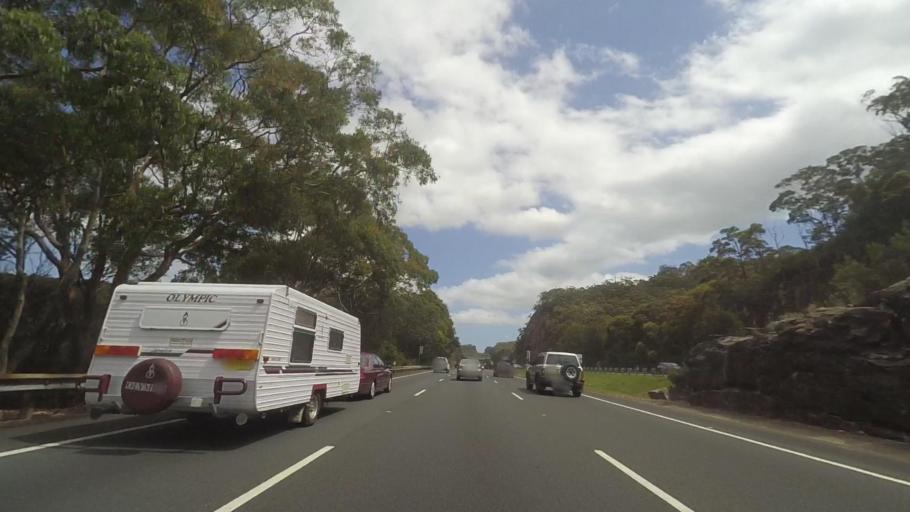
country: AU
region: New South Wales
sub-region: Hornsby Shire
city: Berowra
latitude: -33.5545
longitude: 151.1926
